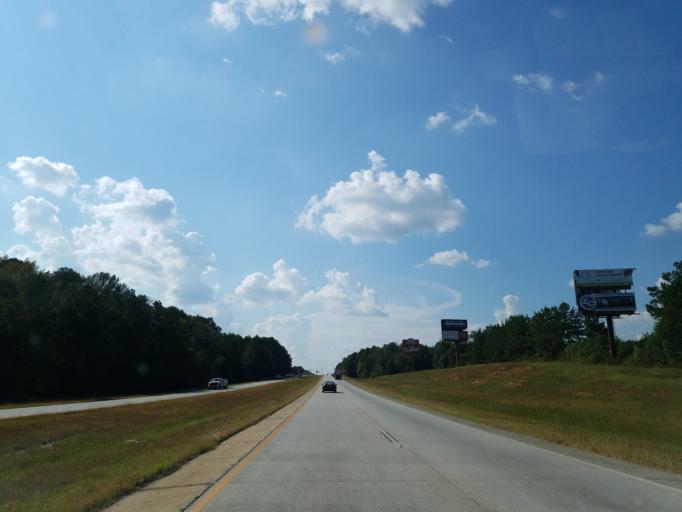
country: US
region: Georgia
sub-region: Barrow County
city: Statham
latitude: 33.9543
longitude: -83.5999
